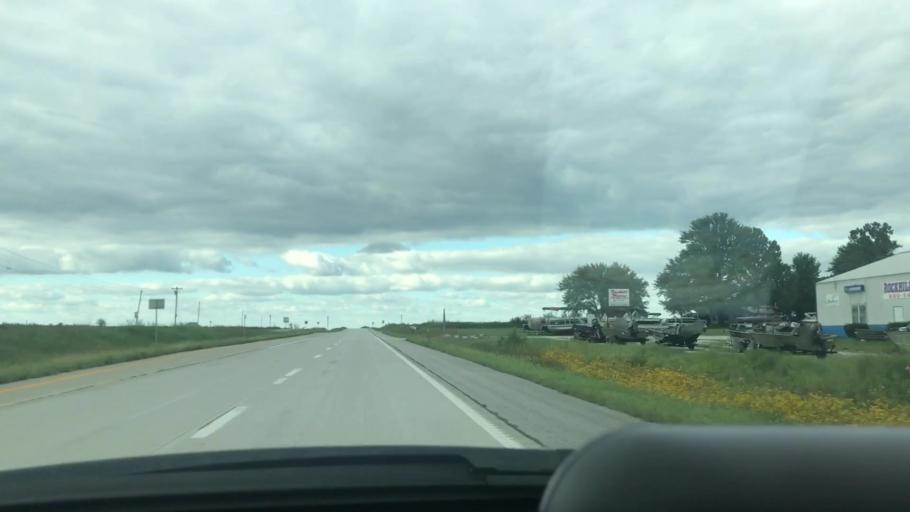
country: US
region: Missouri
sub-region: Benton County
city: Lincoln
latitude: 38.3528
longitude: -93.3395
